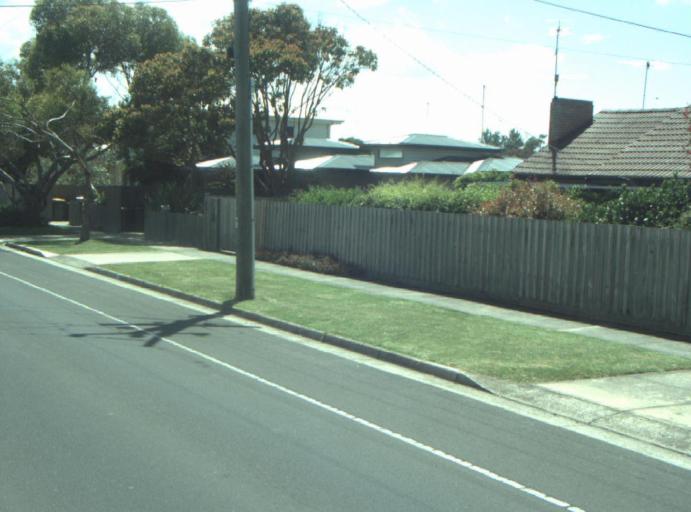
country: AU
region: Victoria
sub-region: Greater Geelong
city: Leopold
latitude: -38.2790
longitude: 144.4877
